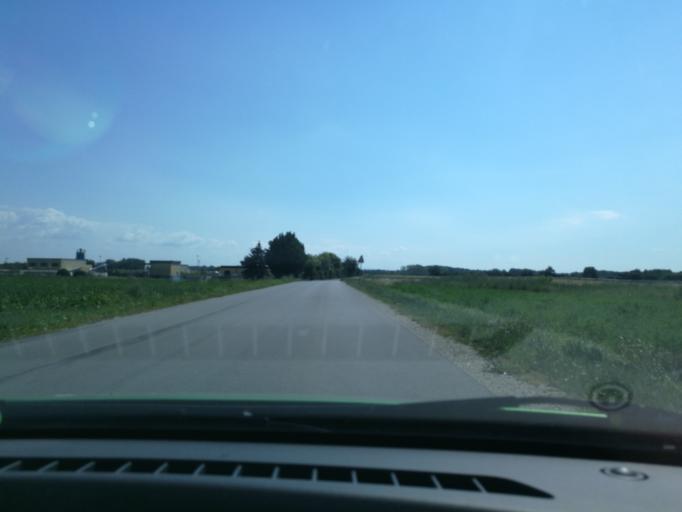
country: AT
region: Lower Austria
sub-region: Politischer Bezirk Ganserndorf
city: Ganserndorf
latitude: 48.3459
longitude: 16.7327
